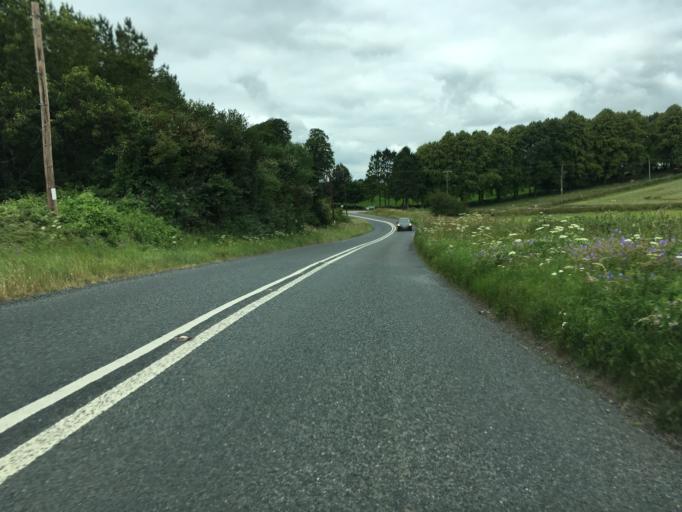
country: GB
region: England
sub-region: Gloucestershire
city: Westfield
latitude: 51.8928
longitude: -1.8718
